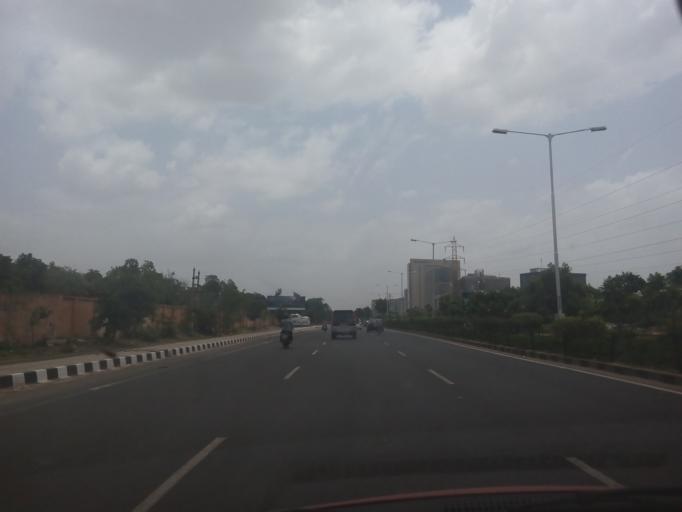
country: IN
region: Gujarat
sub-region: Ahmadabad
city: Sarkhej
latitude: 23.0086
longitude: 72.5014
